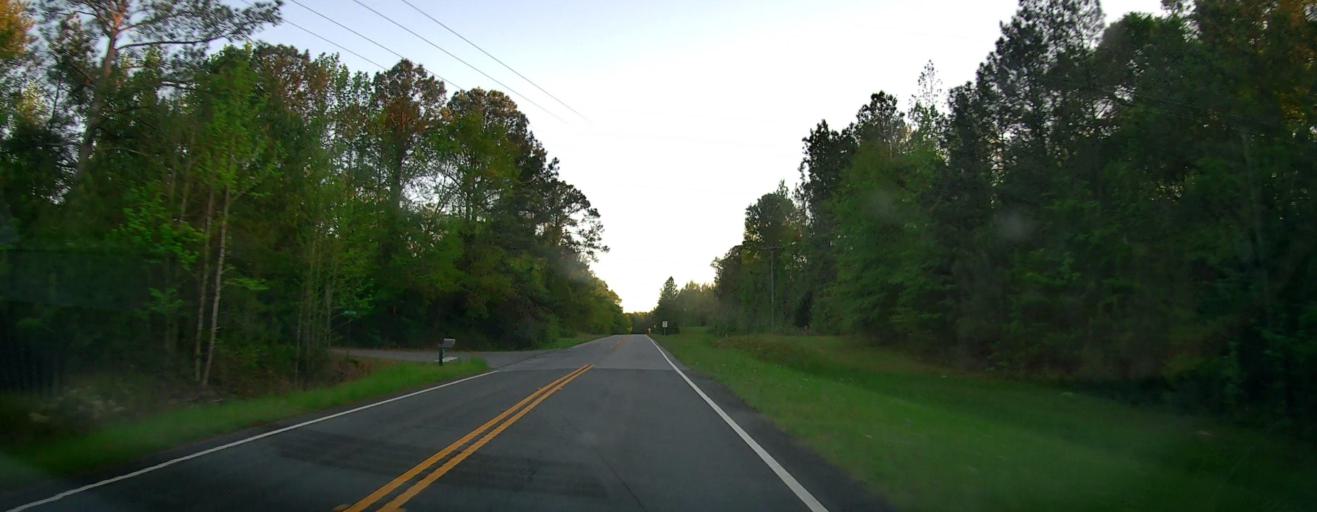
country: US
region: Georgia
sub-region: Talbot County
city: Talbotton
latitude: 32.5304
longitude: -84.6057
